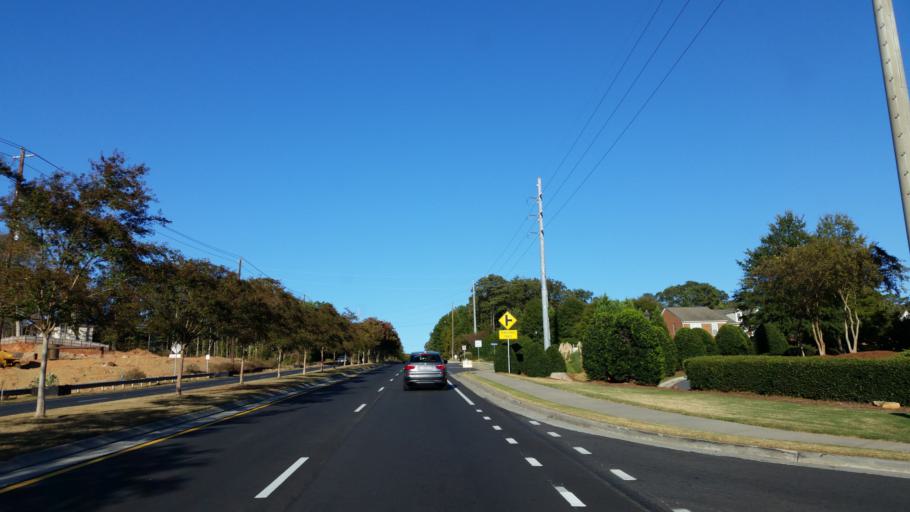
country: US
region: Georgia
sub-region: Fulton County
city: Roswell
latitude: 34.0055
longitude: -84.3895
